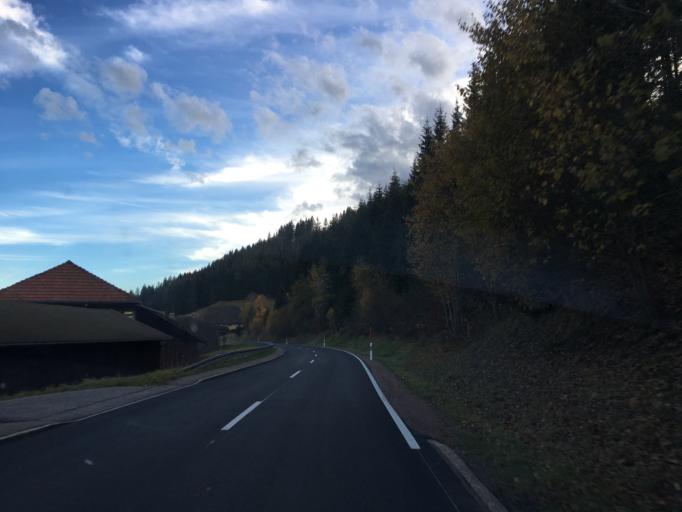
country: DE
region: Baden-Wuerttemberg
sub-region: Freiburg Region
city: Furtwangen im Schwarzwald
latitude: 48.0636
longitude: 8.1956
